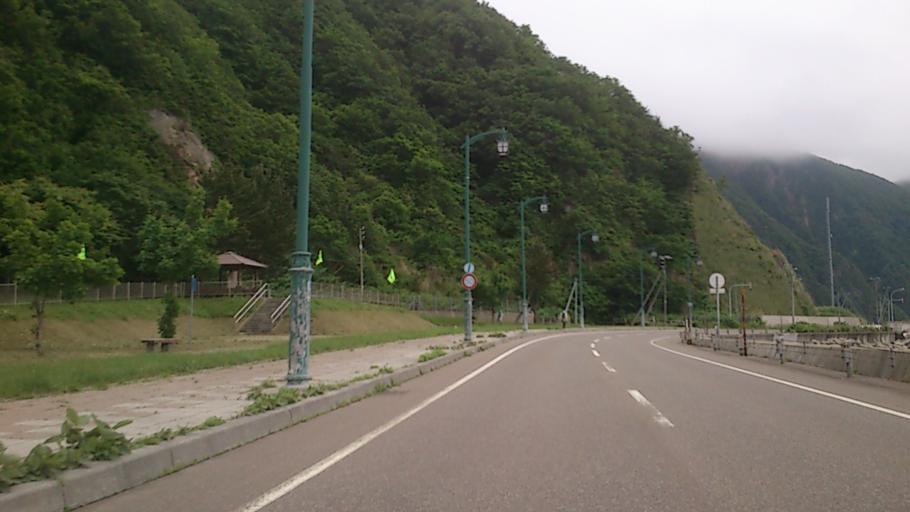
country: JP
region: Hokkaido
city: Kamiiso
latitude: 42.2787
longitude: 139.7851
